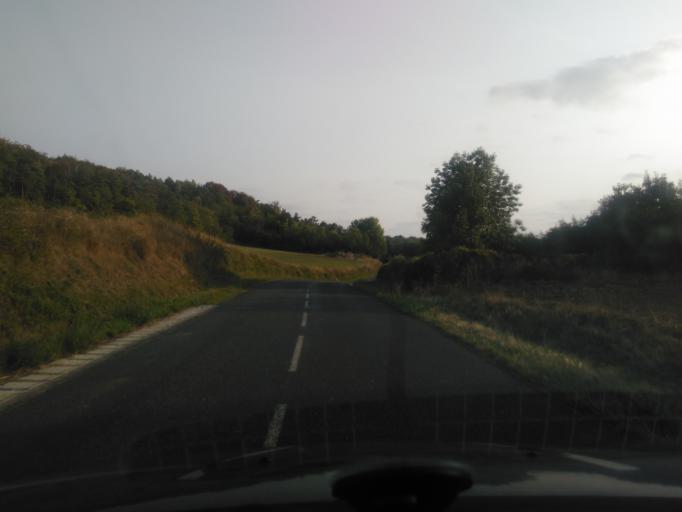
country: FR
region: Champagne-Ardenne
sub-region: Departement de la Marne
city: Fismes
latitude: 49.2528
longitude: 3.6960
